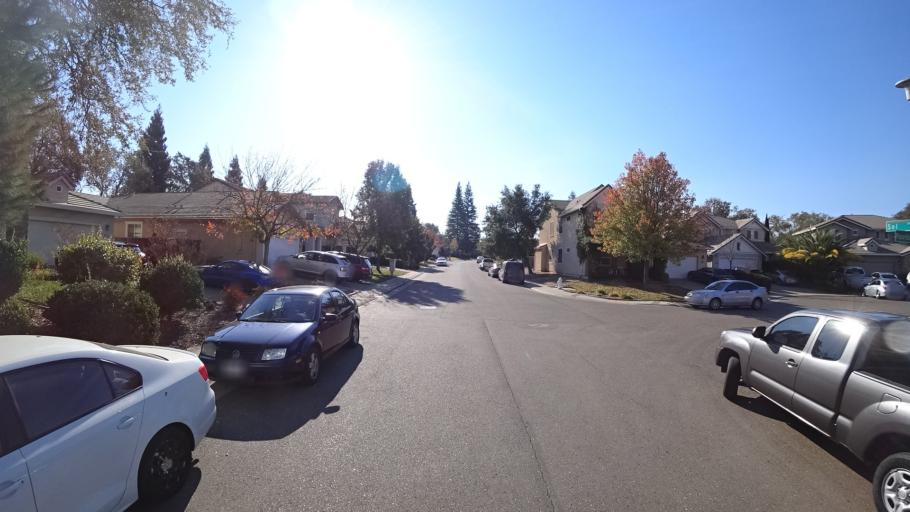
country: US
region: California
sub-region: Sacramento County
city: Citrus Heights
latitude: 38.6831
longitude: -121.2942
